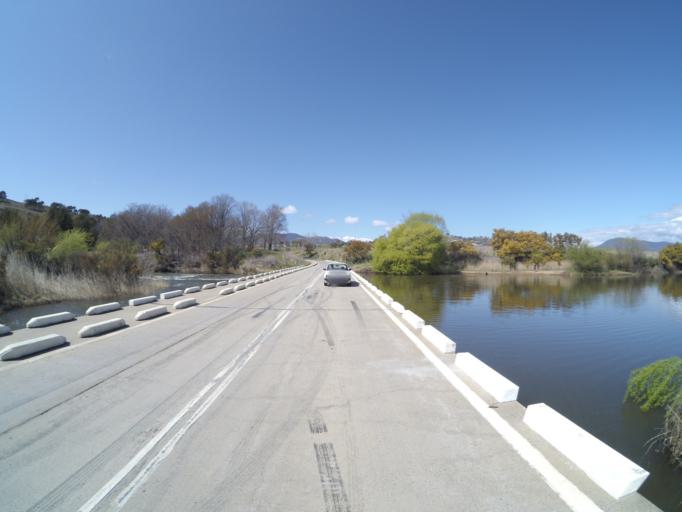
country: AU
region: Australian Capital Territory
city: Macarthur
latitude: -35.4520
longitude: 149.0737
